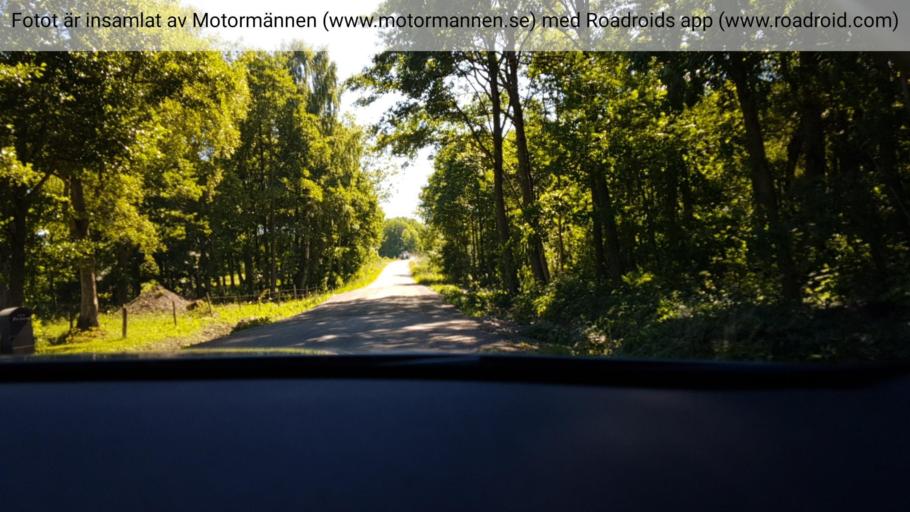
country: SE
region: Vaestra Goetaland
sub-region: Falkopings Kommun
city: Akarp
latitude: 58.1919
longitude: 13.7299
